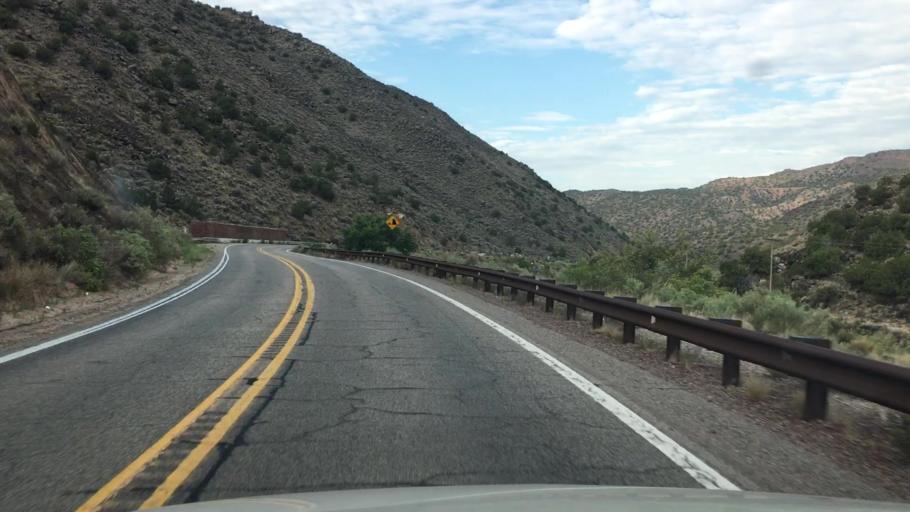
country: US
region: New Mexico
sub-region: Rio Arriba County
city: Ohkay Owingeh
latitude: 36.1989
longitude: -105.9714
